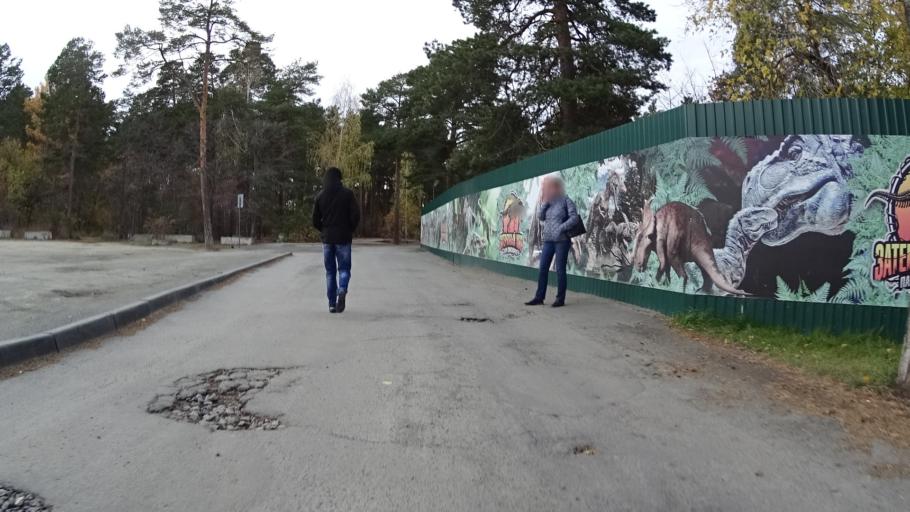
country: RU
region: Chelyabinsk
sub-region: Gorod Chelyabinsk
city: Chelyabinsk
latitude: 55.1664
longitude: 61.3659
